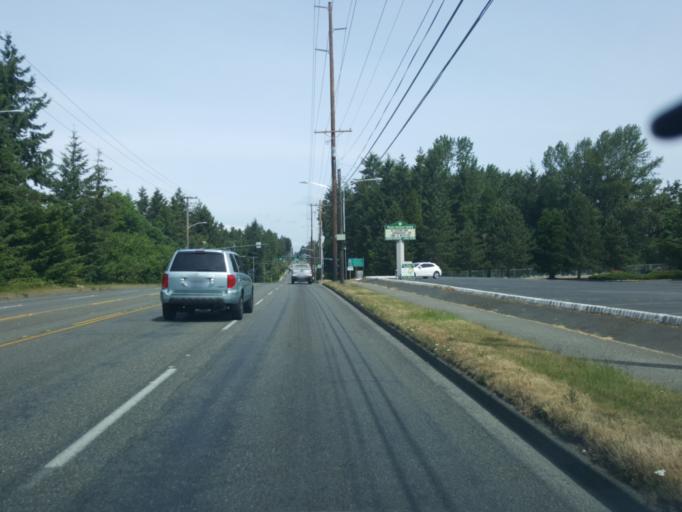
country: US
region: Washington
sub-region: Pierce County
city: Fircrest
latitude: 47.2282
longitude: -122.5051
